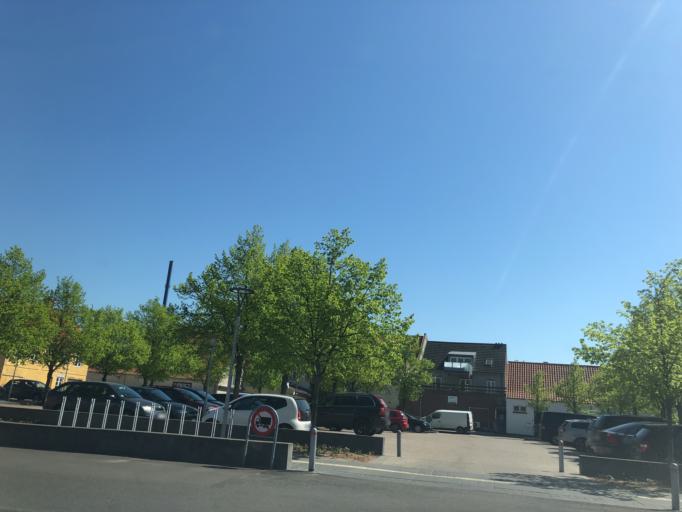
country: DK
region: Zealand
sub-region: Slagelse Kommune
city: Korsor
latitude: 55.3299
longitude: 11.1383
